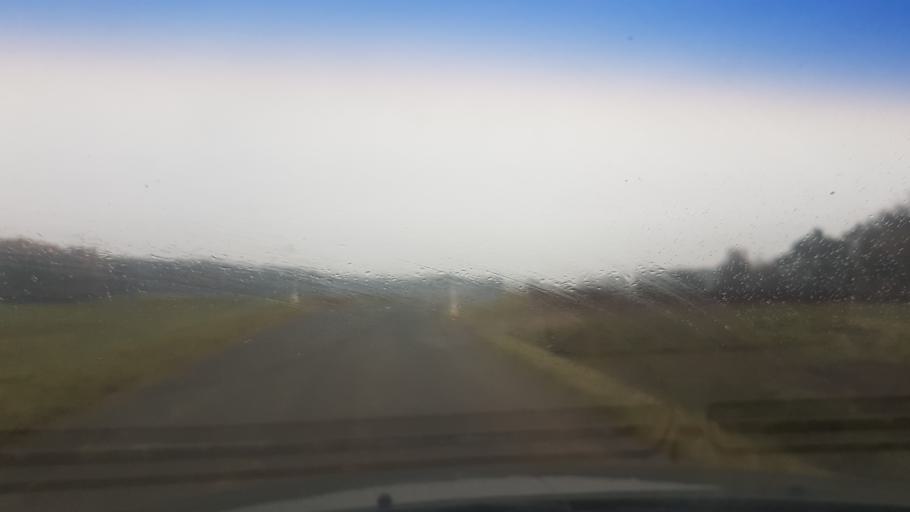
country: DE
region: Bavaria
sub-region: Upper Franconia
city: Weismain
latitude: 50.0559
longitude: 11.2878
